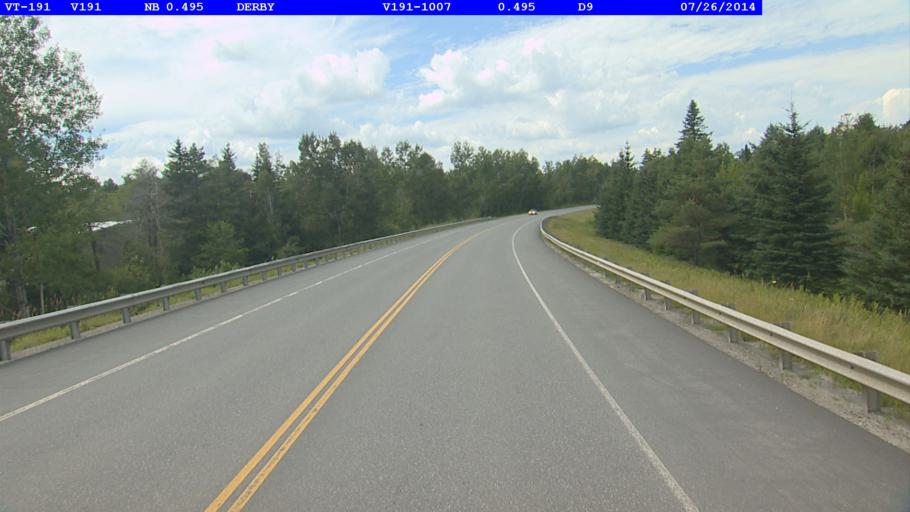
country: US
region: Vermont
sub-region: Orleans County
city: Newport
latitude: 44.9254
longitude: -72.1780
